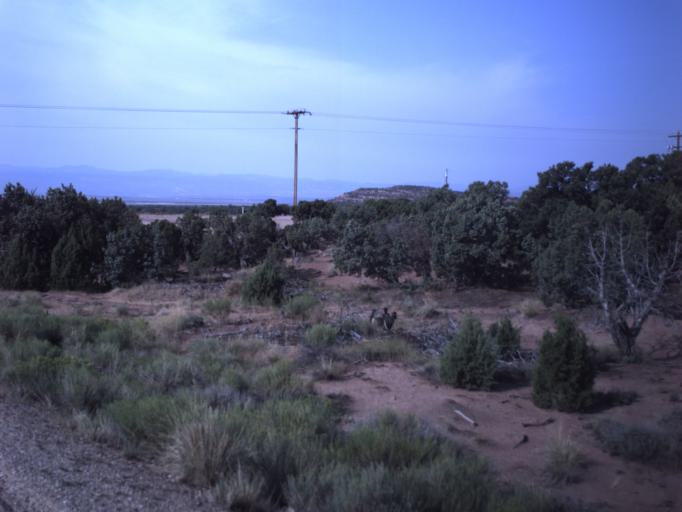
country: US
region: Utah
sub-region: Duchesne County
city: Duchesne
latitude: 40.2956
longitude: -110.3745
